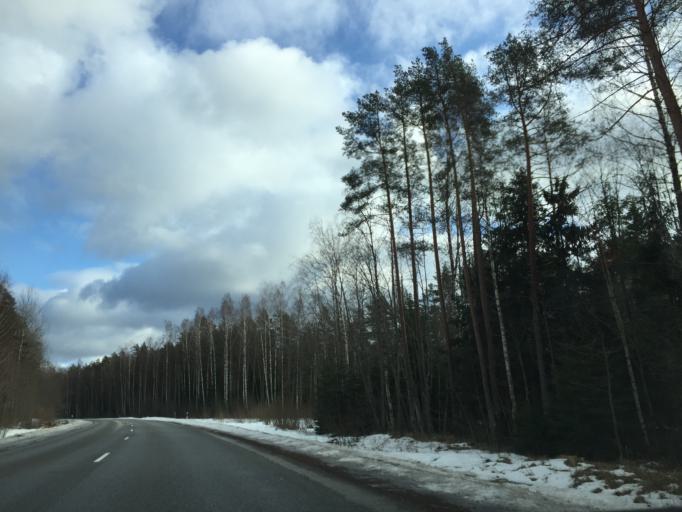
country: LV
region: Aloja
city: Staicele
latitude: 57.8471
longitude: 24.7163
